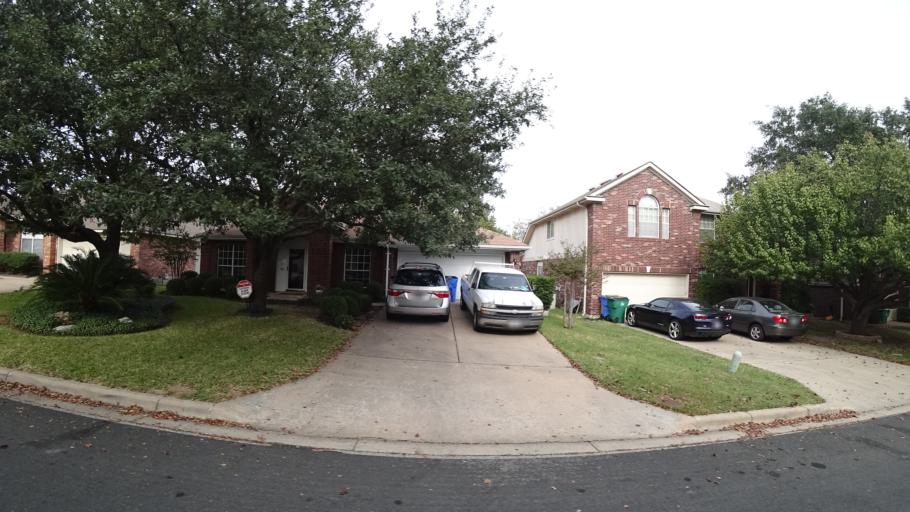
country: US
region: Texas
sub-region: Travis County
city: Wells Branch
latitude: 30.4516
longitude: -97.6762
